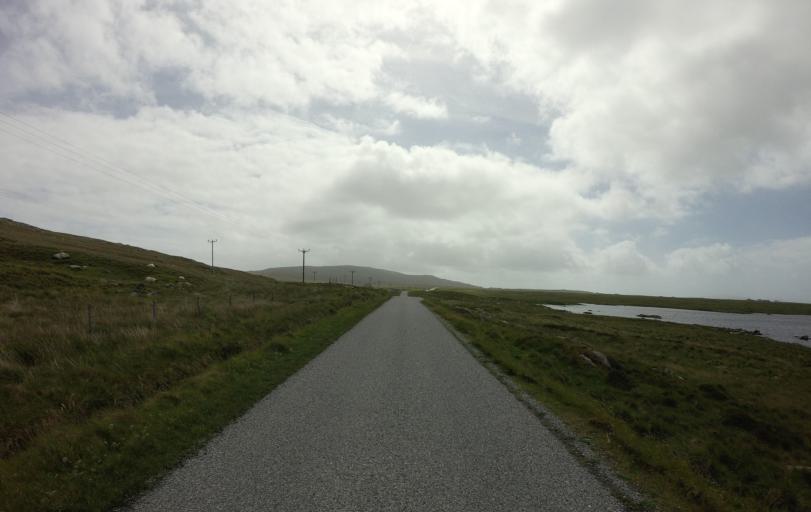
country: GB
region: Scotland
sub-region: Eilean Siar
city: Isle of South Uist
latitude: 57.1431
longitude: -7.3716
